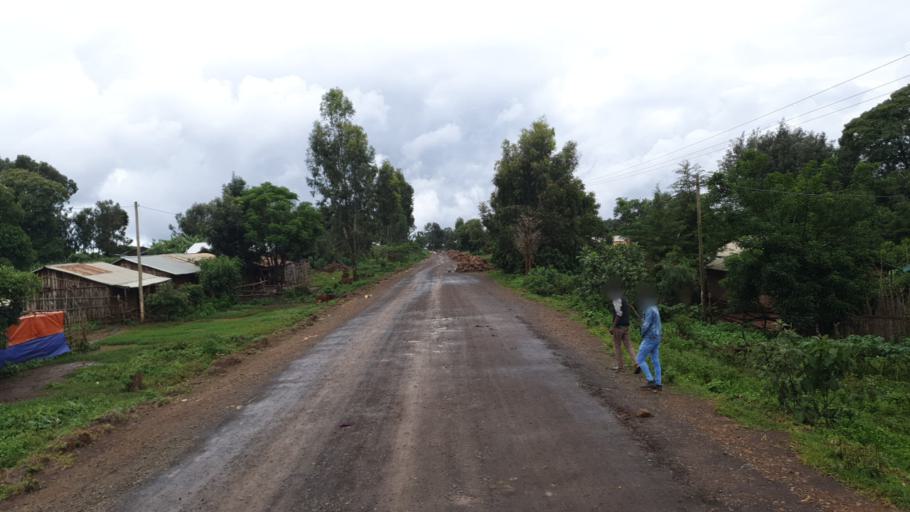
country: ET
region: Amhara
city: Bure
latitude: 10.1367
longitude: 36.9301
